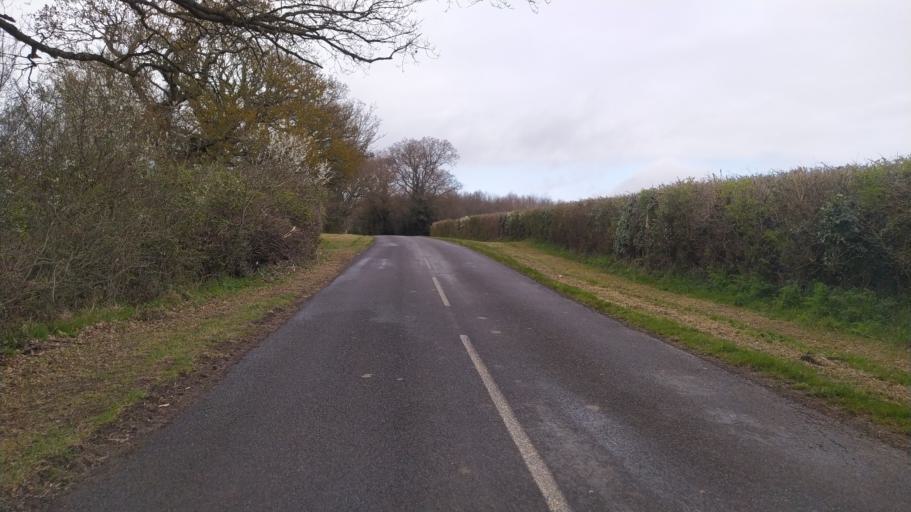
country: GB
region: England
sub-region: West Sussex
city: Petworth
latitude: 51.0094
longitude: -0.6074
